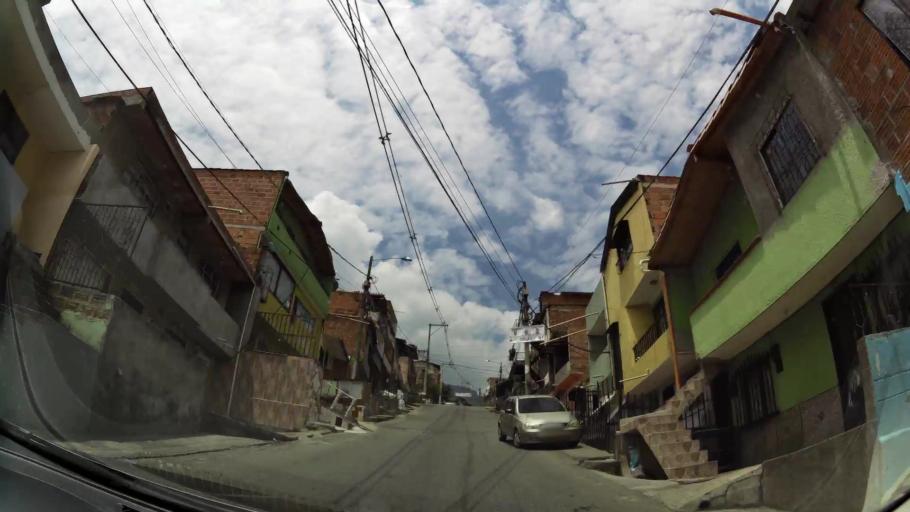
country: CO
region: Antioquia
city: Bello
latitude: 6.3133
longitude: -75.5796
